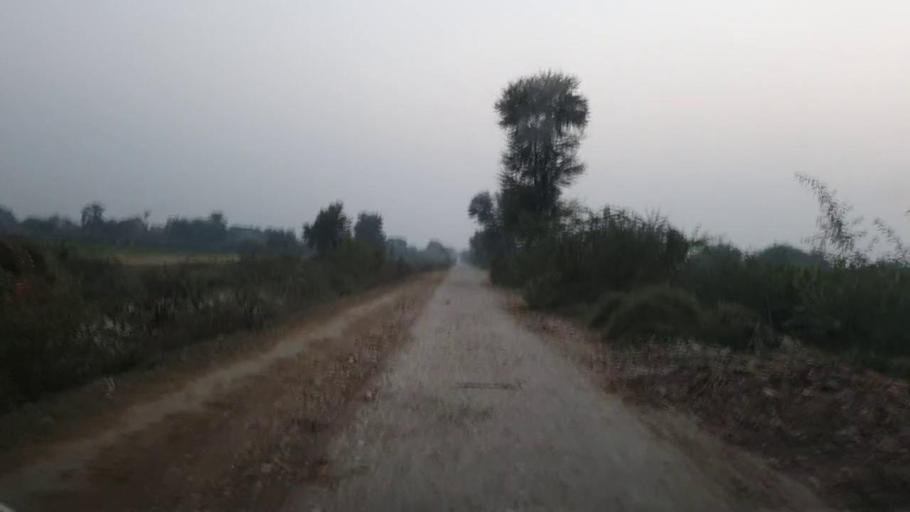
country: PK
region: Sindh
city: Karaundi
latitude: 26.9374
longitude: 68.4435
